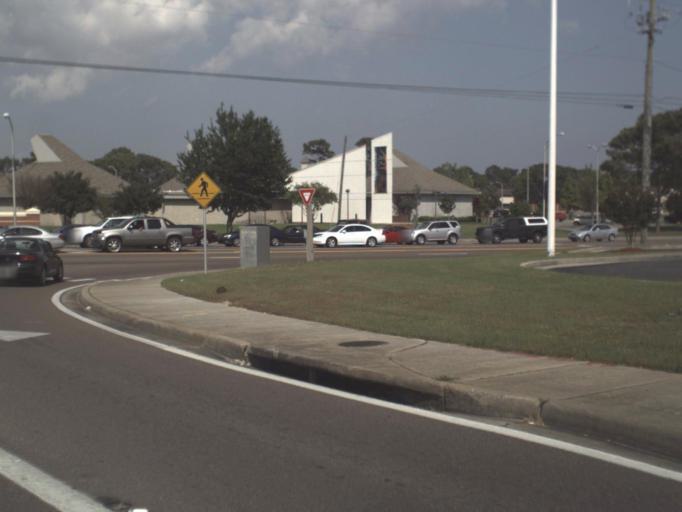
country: US
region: Florida
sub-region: Escambia County
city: Brent
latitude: 30.4790
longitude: -87.2075
